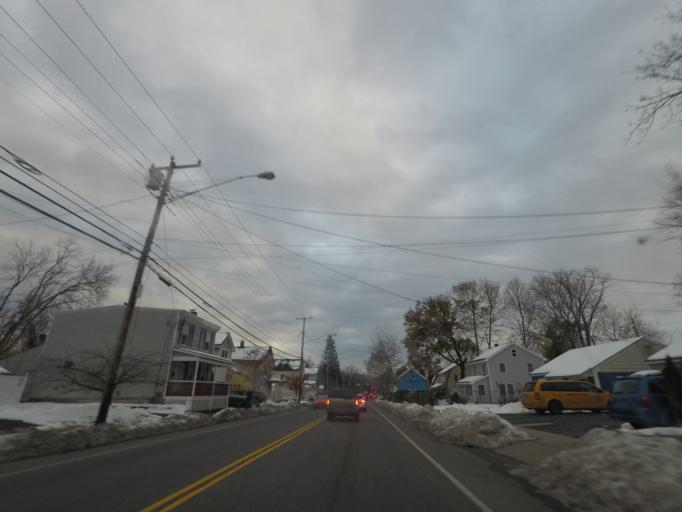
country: US
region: New York
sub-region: Orange County
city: Newburgh
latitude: 41.5099
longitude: -74.0204
